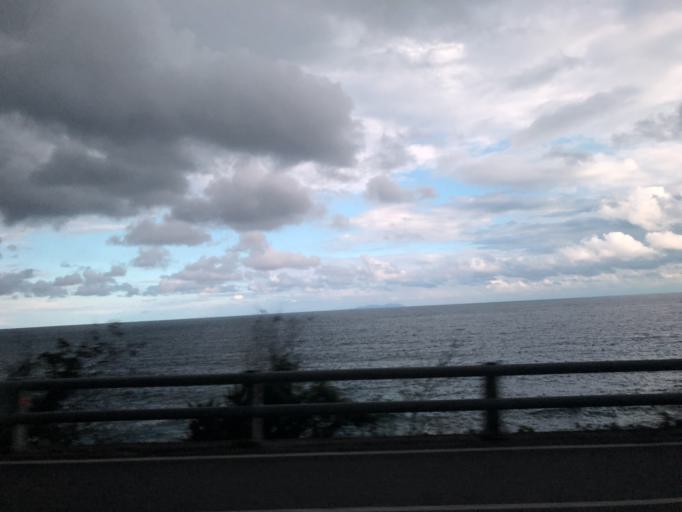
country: TW
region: Taiwan
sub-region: Taitung
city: Taitung
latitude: 22.8587
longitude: 121.1991
